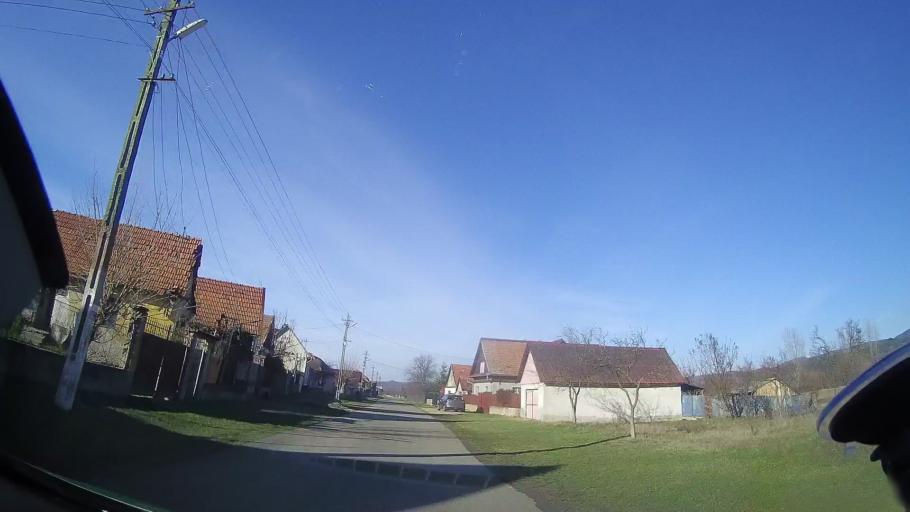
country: RO
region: Bihor
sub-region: Comuna Auseu
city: Auseu
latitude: 47.0219
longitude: 22.4945
